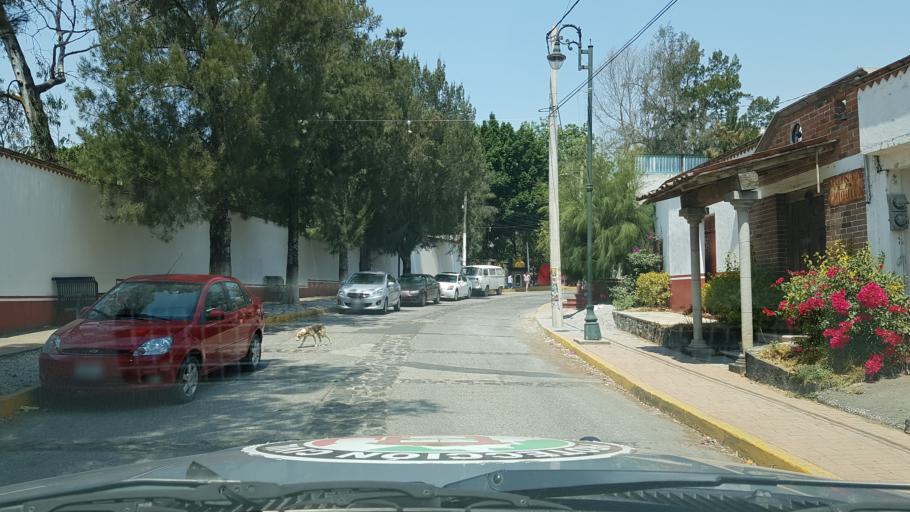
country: MX
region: Mexico
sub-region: Tepetlixpa
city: Nepantla de Sor Juana Ines de la Cruz
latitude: 18.9814
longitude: -98.8418
